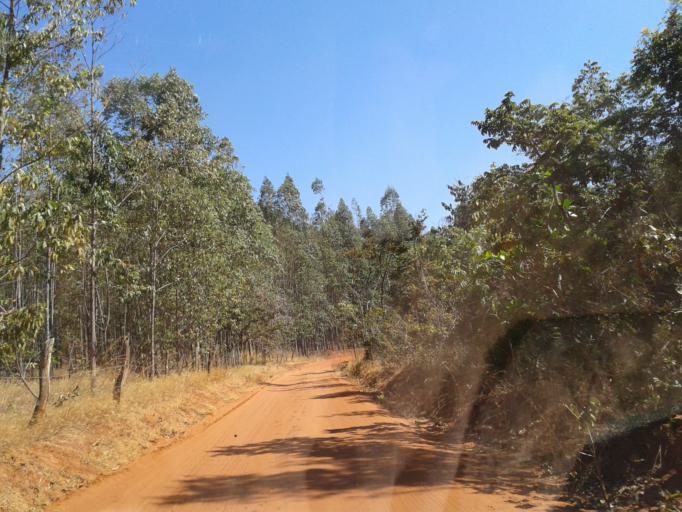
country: BR
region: Minas Gerais
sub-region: Ituiutaba
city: Ituiutaba
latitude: -19.0137
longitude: -49.2191
